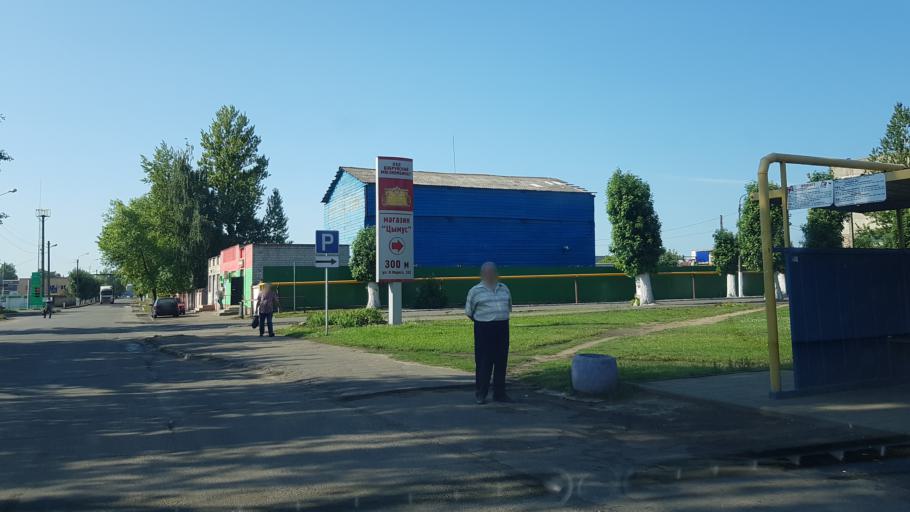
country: BY
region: Mogilev
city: Babruysk
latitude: 53.1328
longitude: 29.1792
